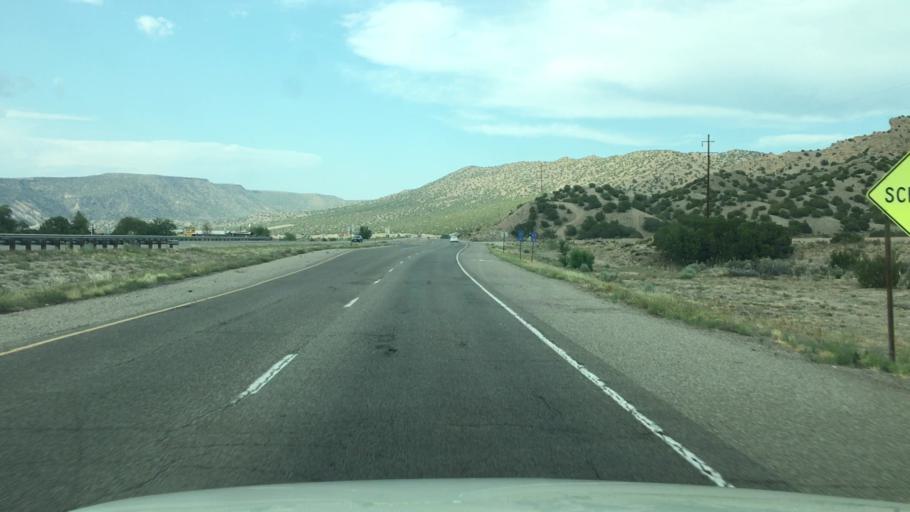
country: US
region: New Mexico
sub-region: Rio Arriba County
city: Ohkay Owingeh
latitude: 36.1457
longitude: -105.9821
